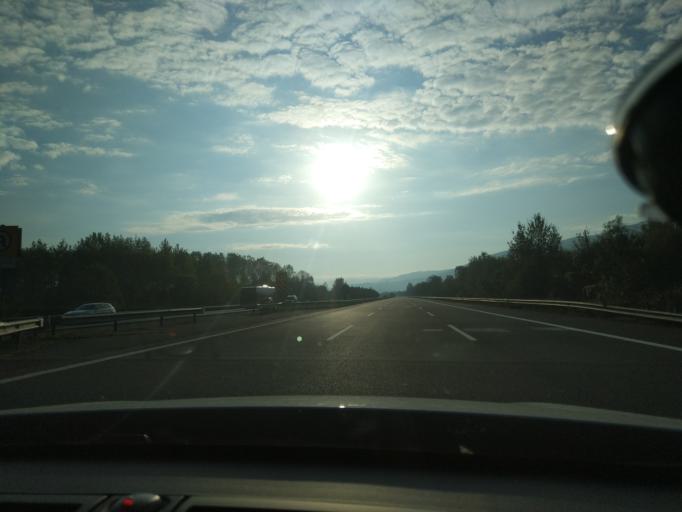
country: TR
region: Duzce
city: Duzce
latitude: 40.7976
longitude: 31.1899
